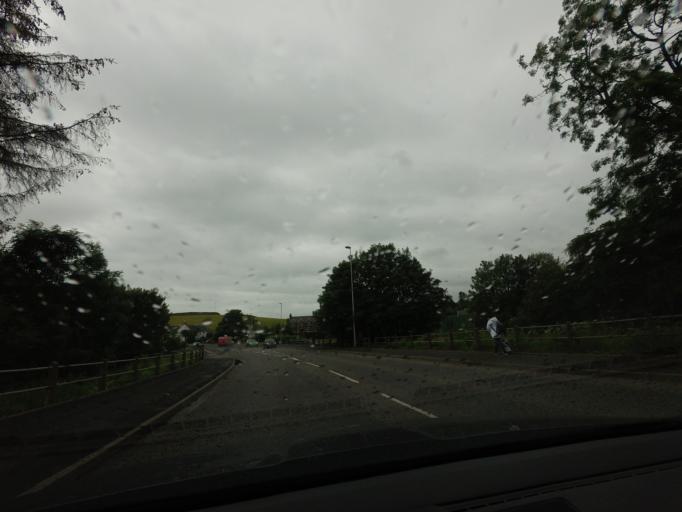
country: GB
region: Scotland
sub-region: Aberdeenshire
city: Turriff
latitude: 57.5341
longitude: -2.4620
